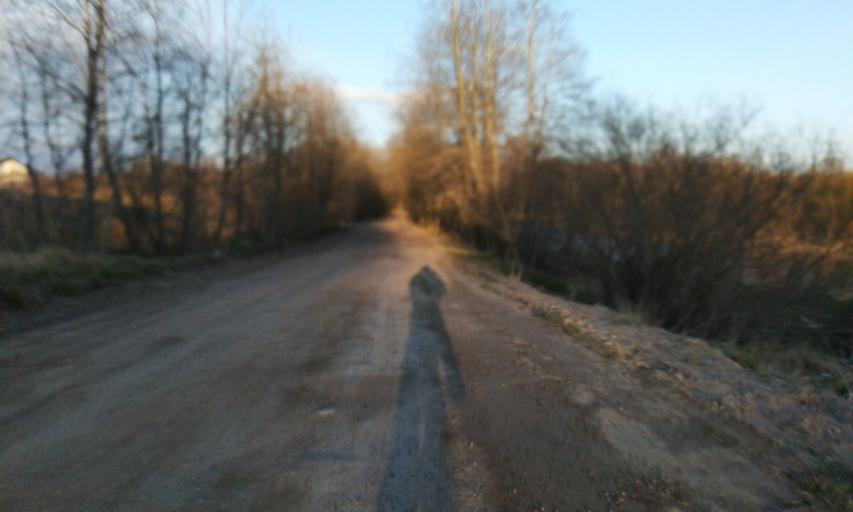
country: RU
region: Leningrad
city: Novoye Devyatkino
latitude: 60.0932
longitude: 30.4531
